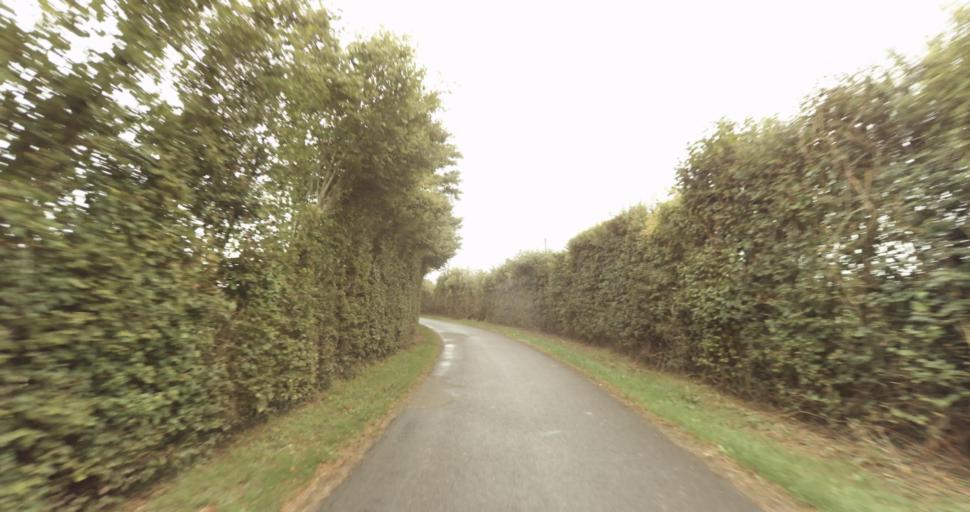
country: FR
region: Lower Normandy
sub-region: Departement de l'Orne
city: Sainte-Gauburge-Sainte-Colombe
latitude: 48.7303
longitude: 0.3685
